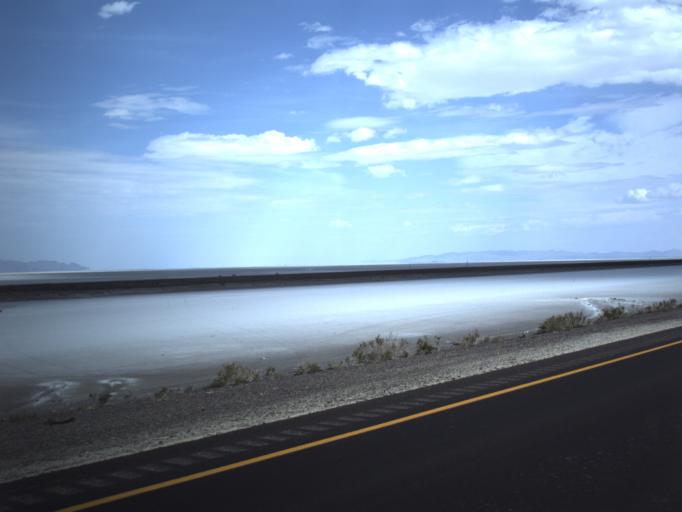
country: US
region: Utah
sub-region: Tooele County
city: Wendover
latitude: 40.7340
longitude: -113.6368
